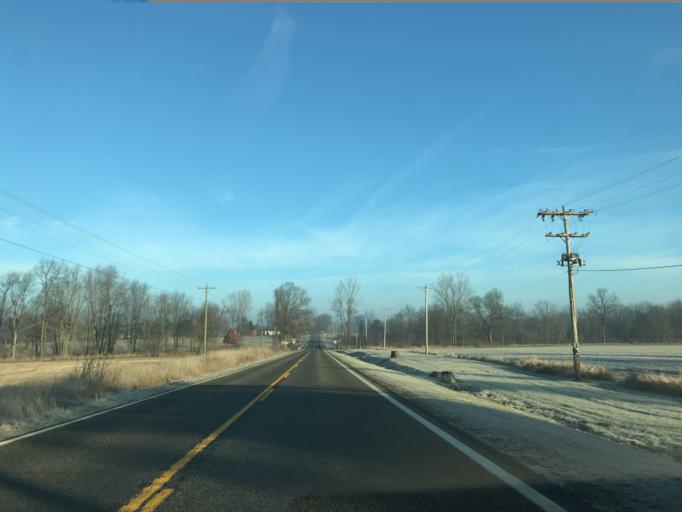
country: US
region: Michigan
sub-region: Eaton County
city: Eaton Rapids
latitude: 42.4791
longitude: -84.6009
